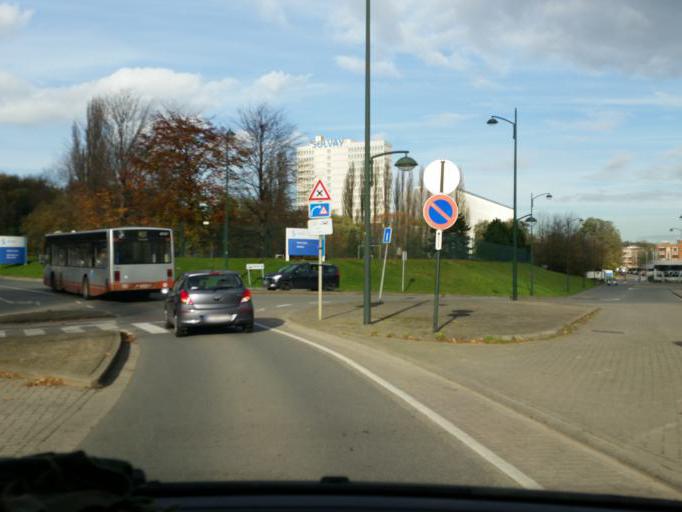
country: BE
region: Flanders
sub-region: Provincie Vlaams-Brabant
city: Diegem
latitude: 50.8995
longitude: 4.3991
